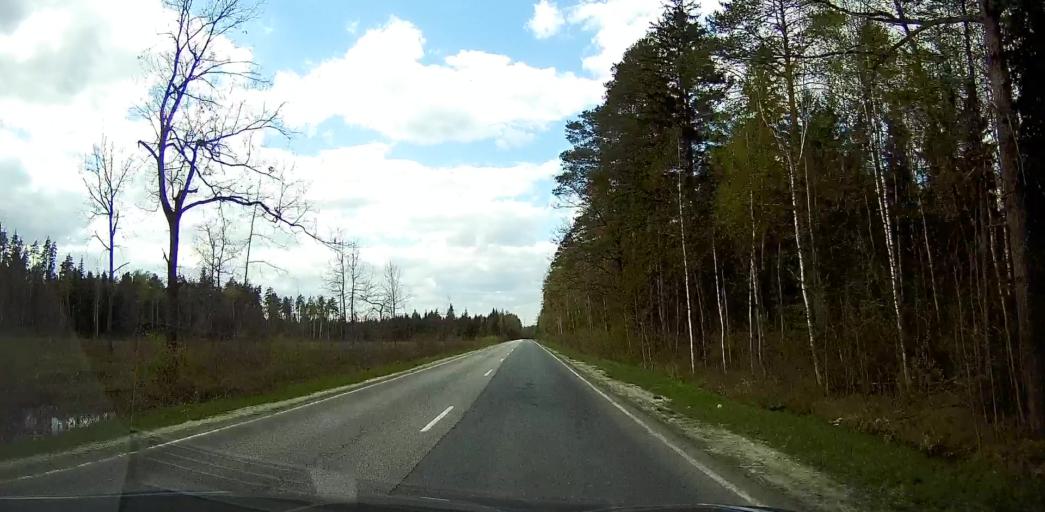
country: RU
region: Moskovskaya
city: Rakhmanovo
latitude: 55.6479
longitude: 38.6696
